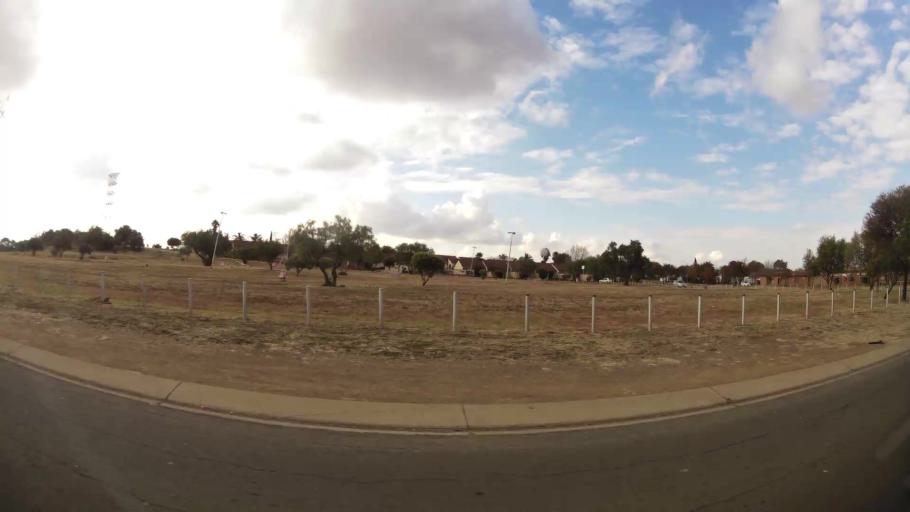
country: ZA
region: Orange Free State
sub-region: Mangaung Metropolitan Municipality
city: Bloemfontein
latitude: -29.0761
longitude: 26.1954
